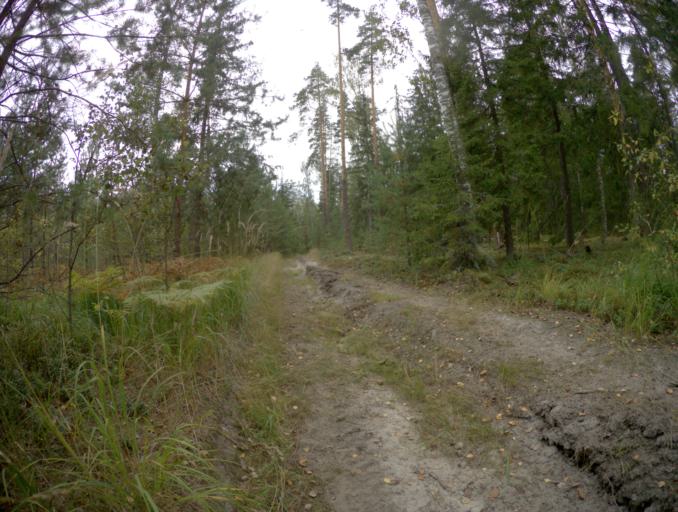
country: RU
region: Vladimir
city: Urshel'skiy
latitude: 55.8198
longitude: 40.2720
